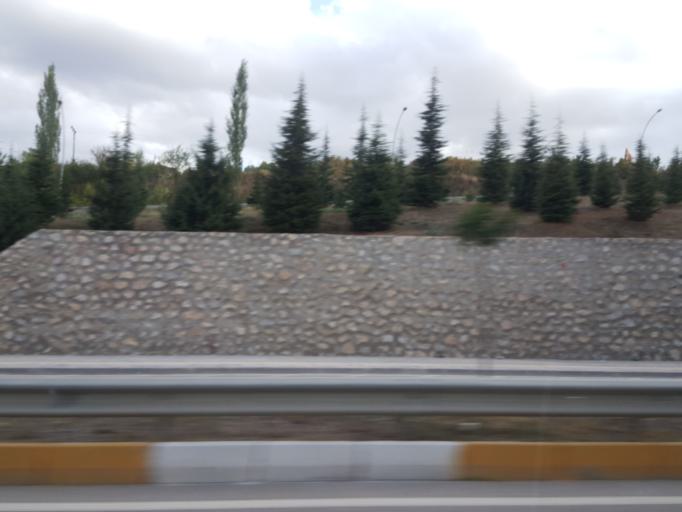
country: TR
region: Tokat
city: Tokat
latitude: 40.3353
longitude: 36.4832
